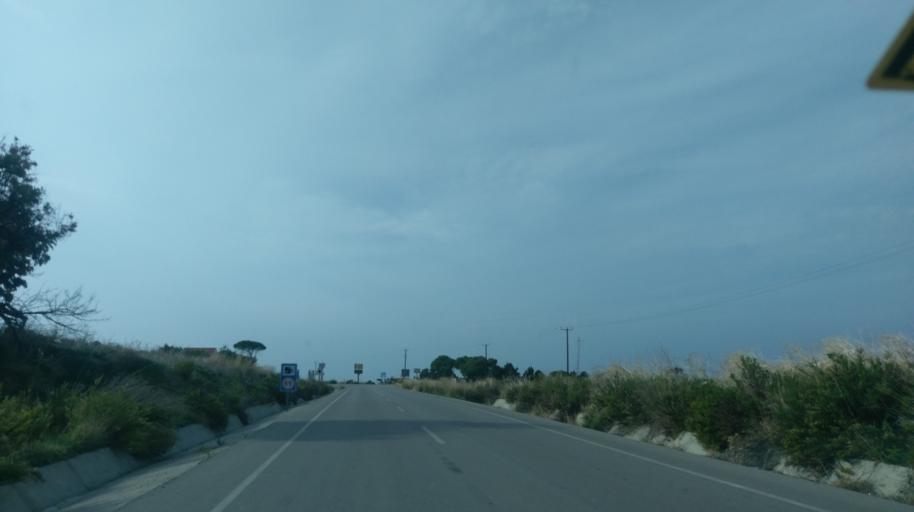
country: CY
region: Ammochostos
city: Trikomo
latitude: 35.4265
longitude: 33.9077
